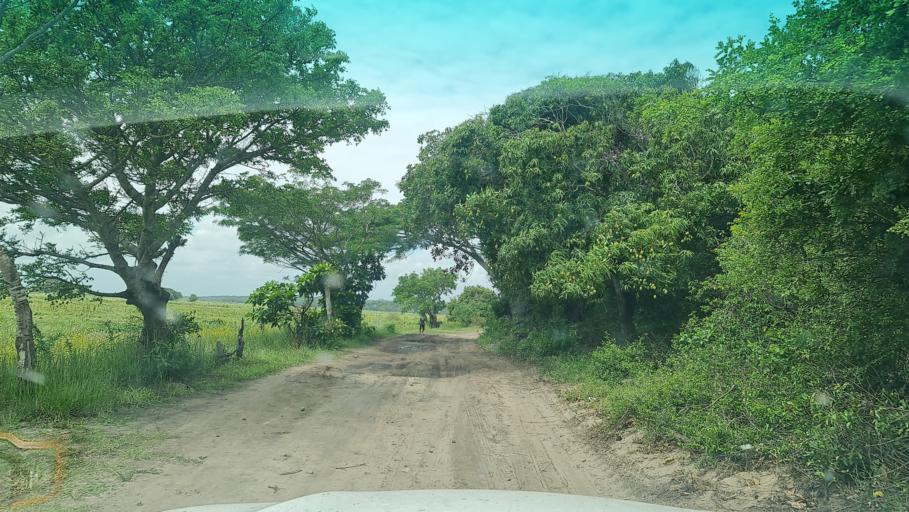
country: MZ
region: Maputo
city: Manhica
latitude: -25.5209
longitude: 32.8632
